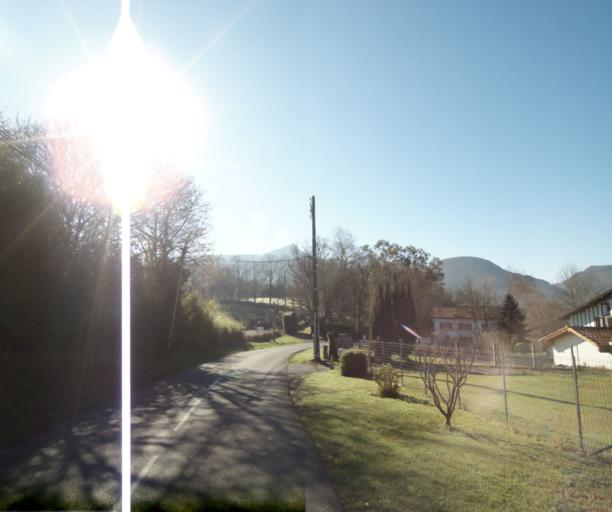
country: FR
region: Aquitaine
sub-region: Departement des Pyrenees-Atlantiques
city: Urrugne
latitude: 43.3458
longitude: -1.6668
